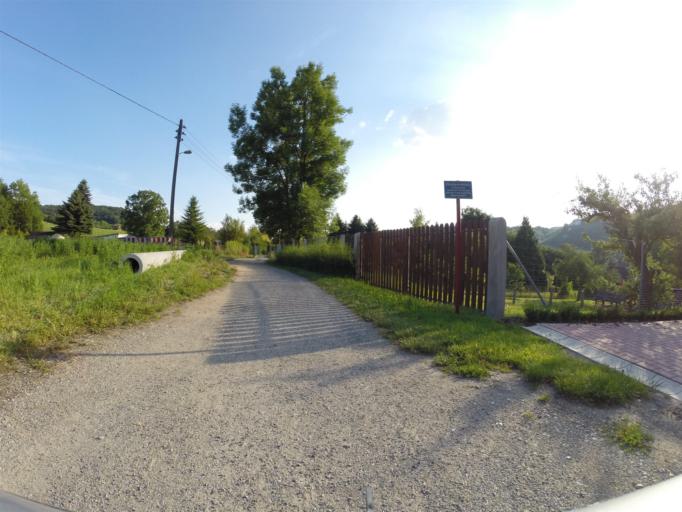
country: DE
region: Thuringia
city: Wichmar
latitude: 51.0057
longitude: 11.6790
